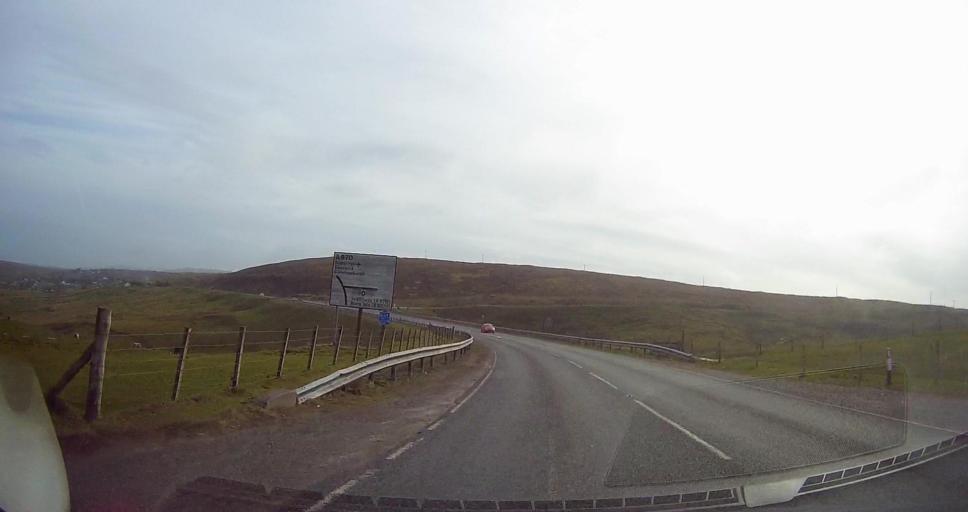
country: GB
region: Scotland
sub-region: Shetland Islands
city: Lerwick
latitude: 60.1390
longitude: -1.2103
